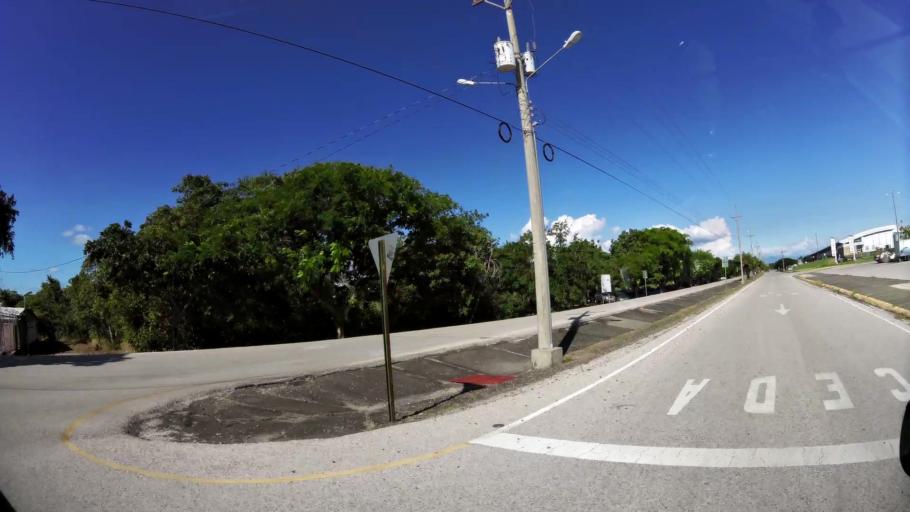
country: CR
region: Guanacaste
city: Liberia
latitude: 10.6004
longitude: -85.5391
